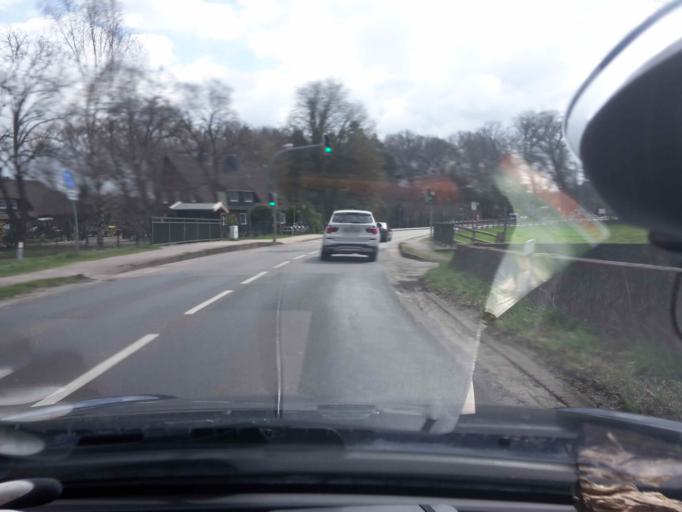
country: DE
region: Lower Saxony
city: Buchholz in der Nordheide
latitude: 53.3144
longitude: 9.9064
